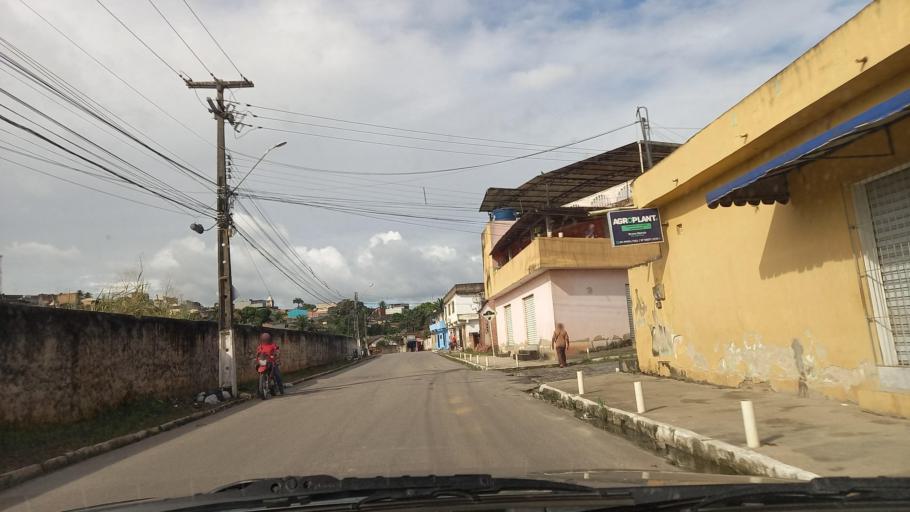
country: BR
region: Pernambuco
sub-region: Palmares
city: Palmares
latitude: -8.6824
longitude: -35.5958
